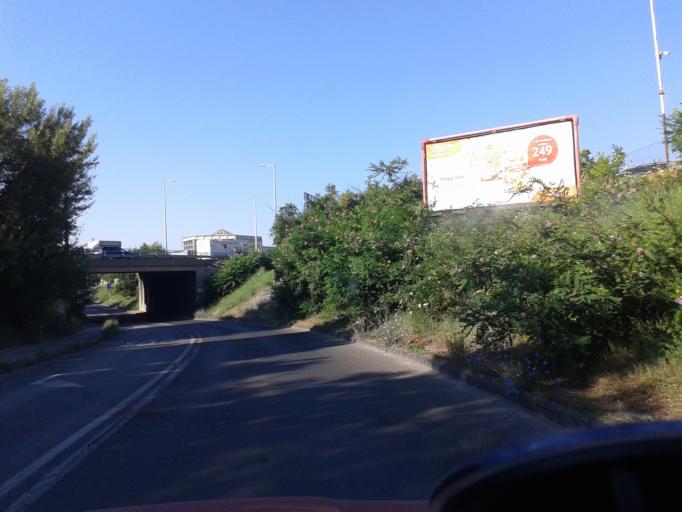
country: HU
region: Budapest
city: Budapest XI. keruelet
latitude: 47.4648
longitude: 19.0124
